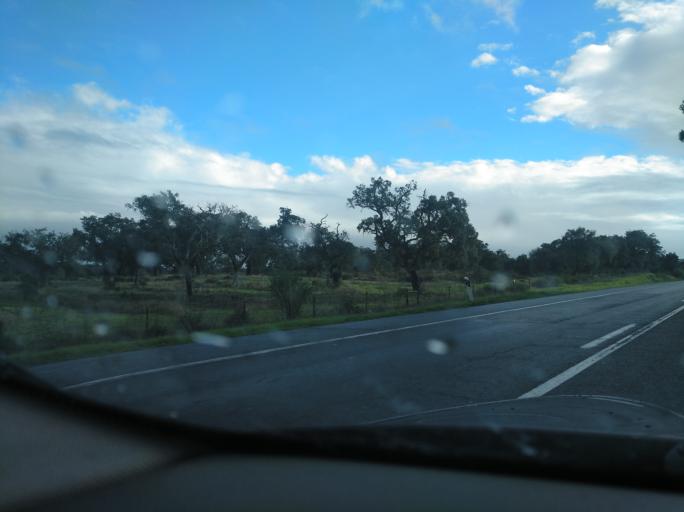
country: PT
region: Setubal
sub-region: Grandola
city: Grandola
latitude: 38.0271
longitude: -8.3997
